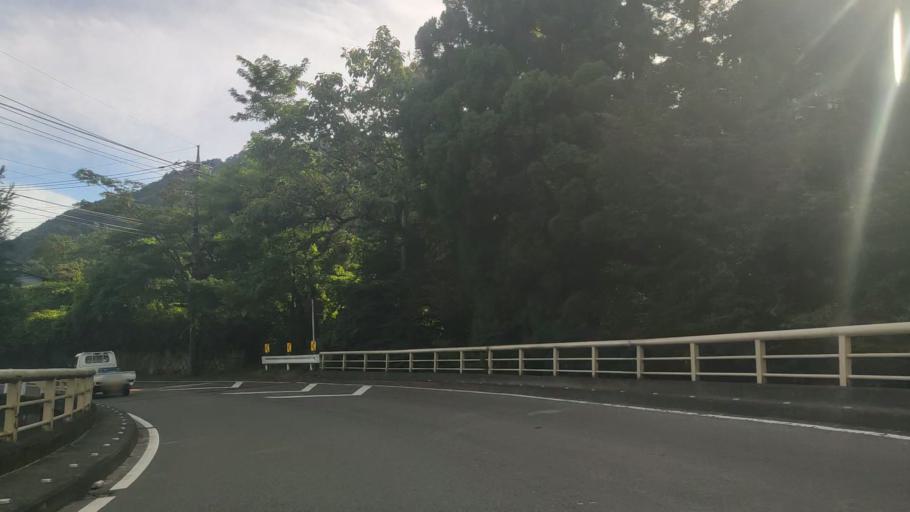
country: JP
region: Gunma
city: Omamacho-omama
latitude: 36.5562
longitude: 139.3733
